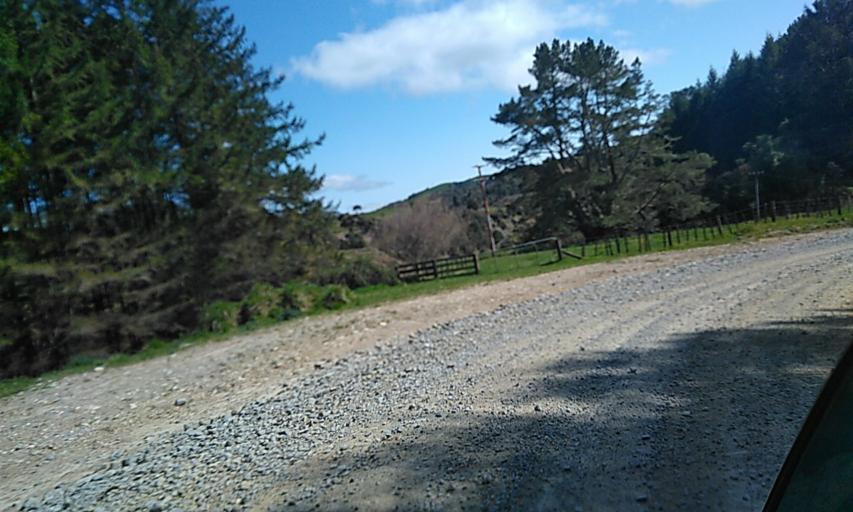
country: NZ
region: Gisborne
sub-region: Gisborne District
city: Gisborne
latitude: -38.2155
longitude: 178.0673
